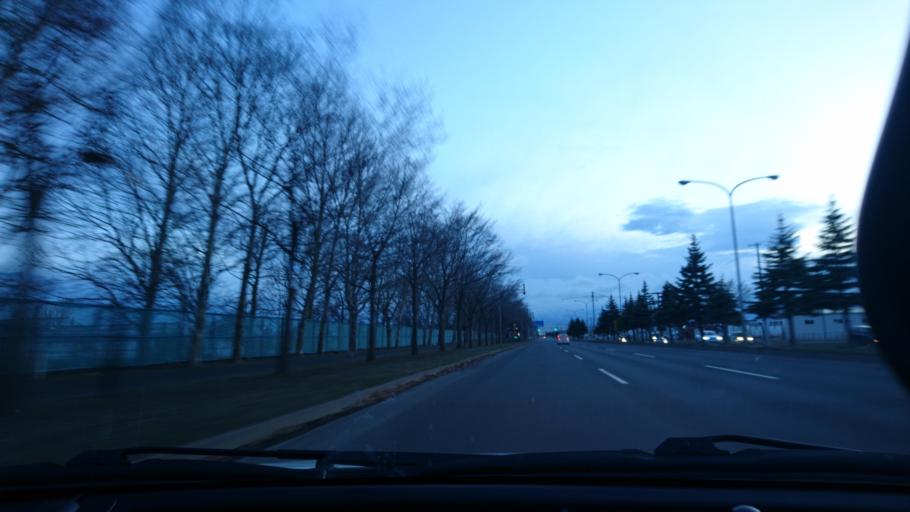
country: JP
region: Hokkaido
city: Sapporo
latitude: 43.1191
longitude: 141.4097
